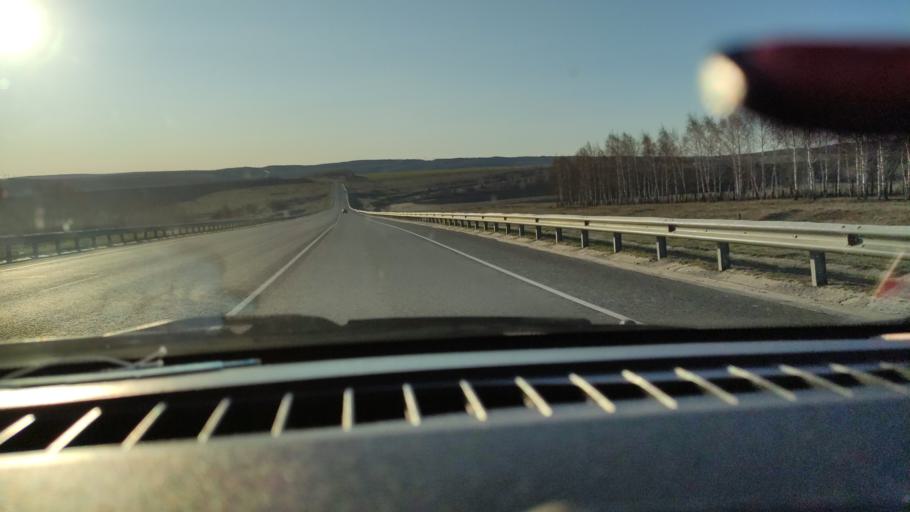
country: RU
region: Saratov
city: Shikhany
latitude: 52.1199
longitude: 47.2673
